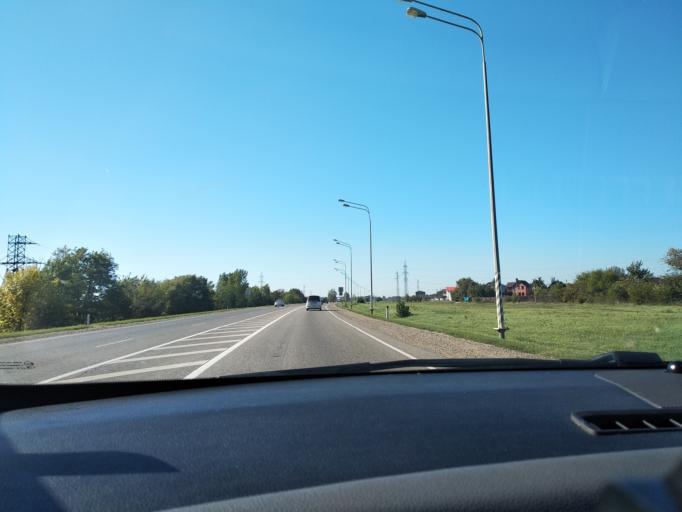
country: RU
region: Krasnodarskiy
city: Agronom
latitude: 45.1620
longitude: 39.0819
